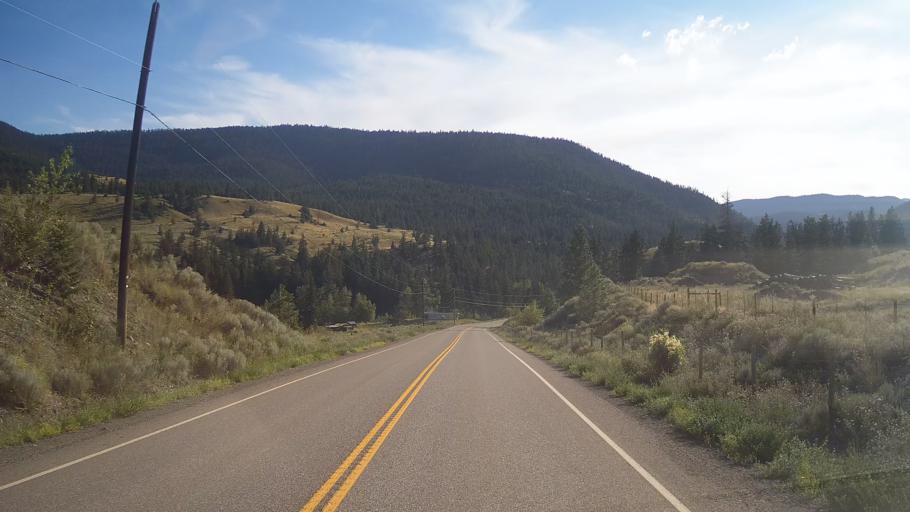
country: CA
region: British Columbia
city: Cache Creek
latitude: 50.8859
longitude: -121.4689
